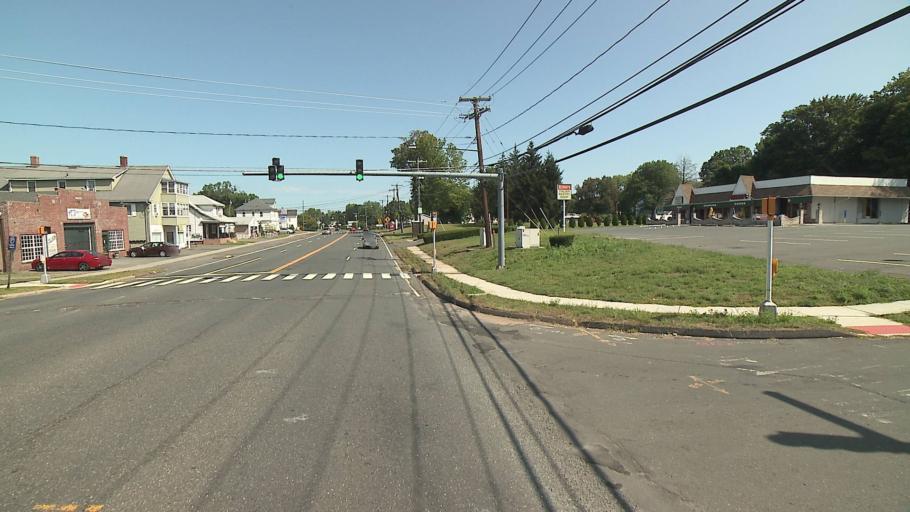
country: US
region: Connecticut
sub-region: Hartford County
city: Thompsonville
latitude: 42.0024
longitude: -72.5932
